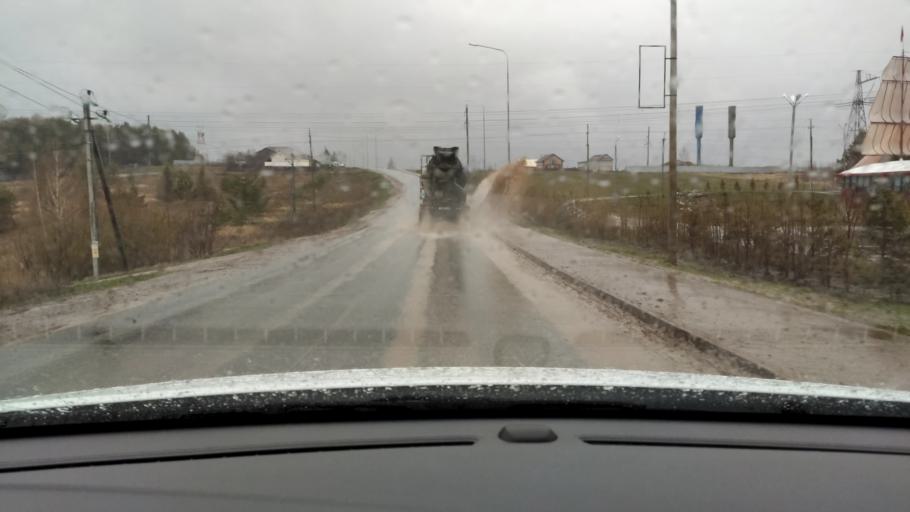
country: RU
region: Tatarstan
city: Vysokaya Gora
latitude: 55.9082
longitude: 49.3168
